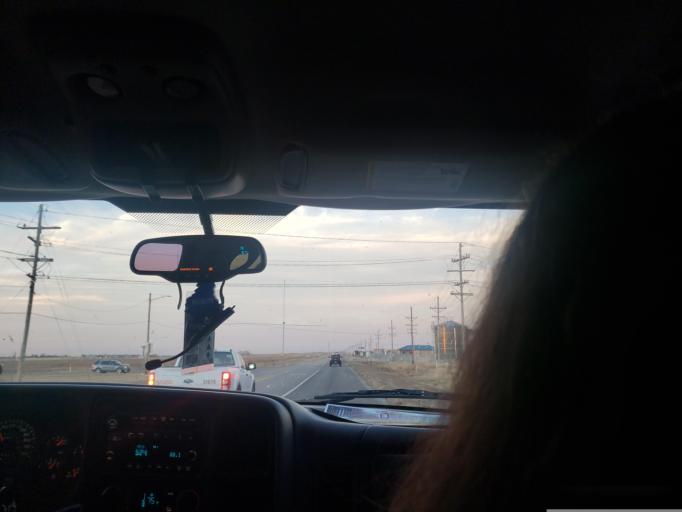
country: US
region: Kansas
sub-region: Seward County
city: Liberal
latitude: 37.0531
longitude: -100.9043
